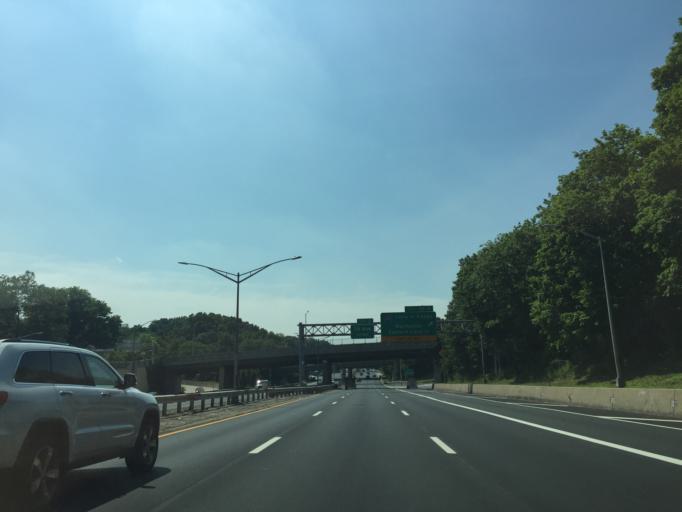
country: US
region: New York
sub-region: Nassau County
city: East Atlantic Beach
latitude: 40.7466
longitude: -73.7728
